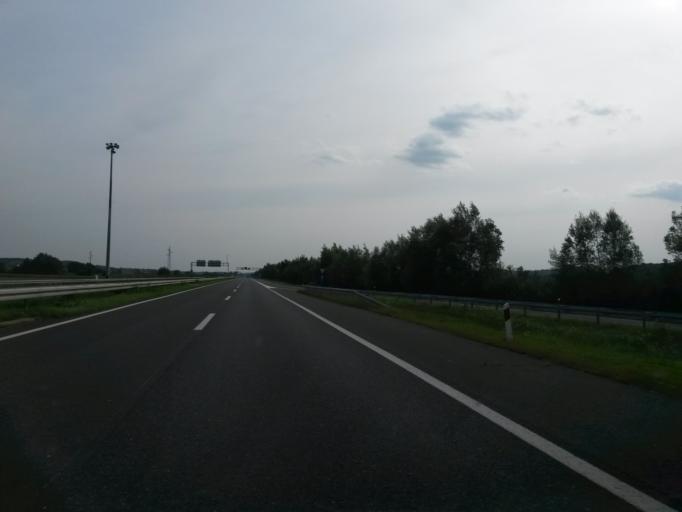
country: HR
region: Zagrebacka
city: Brckovljani
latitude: 45.9922
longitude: 16.2864
